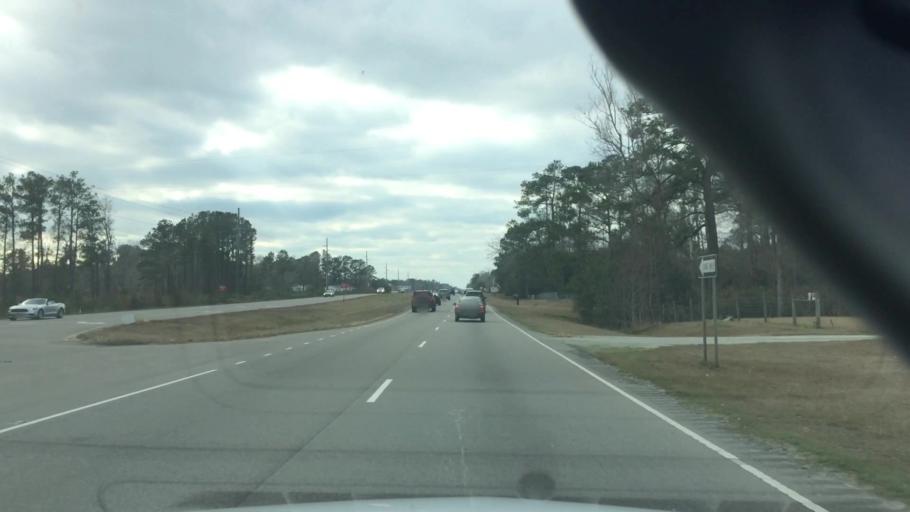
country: US
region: North Carolina
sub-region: Brunswick County
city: Shallotte
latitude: 34.0158
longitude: -78.2775
